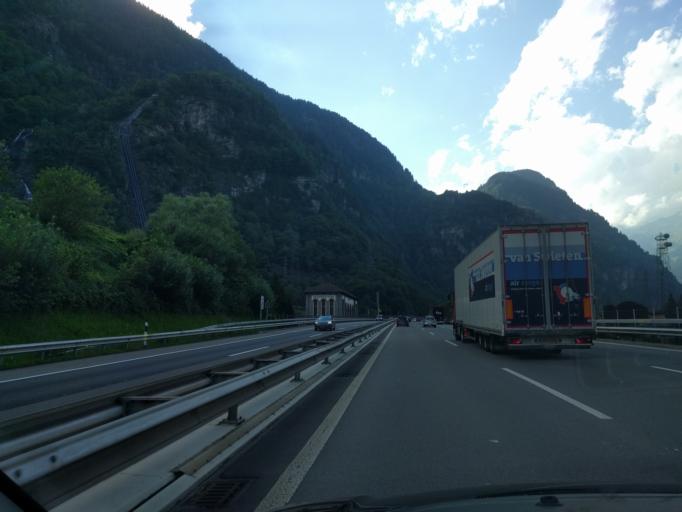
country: CH
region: Ticino
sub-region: Leventina District
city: Faido
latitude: 46.4373
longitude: 8.8431
